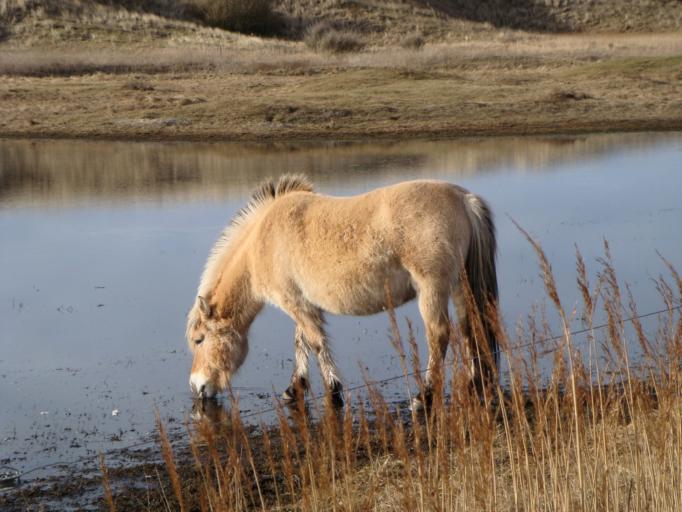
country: NL
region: North Holland
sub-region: Gemeente Texel
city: Den Burg
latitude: 53.0414
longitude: 4.7179
